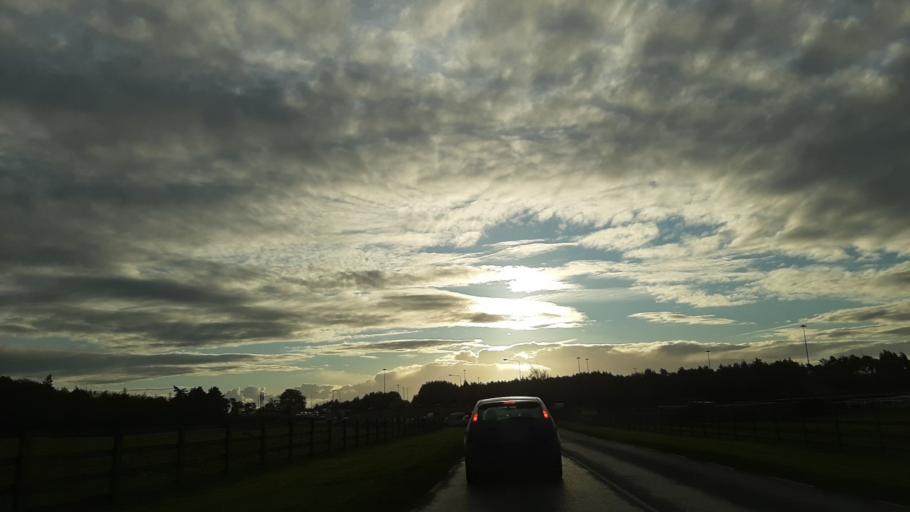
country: IE
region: Leinster
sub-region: Kildare
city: Athgarvan
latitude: 53.1638
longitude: -6.8300
